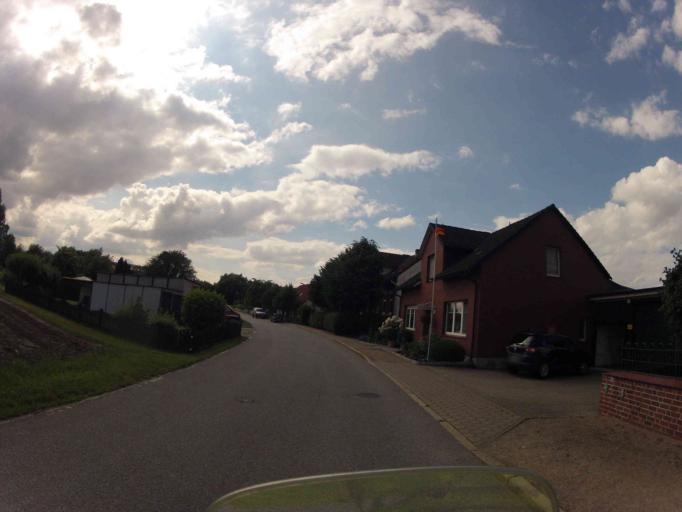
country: DE
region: Hamburg
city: Rothenburgsort
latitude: 53.5140
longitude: 10.0786
